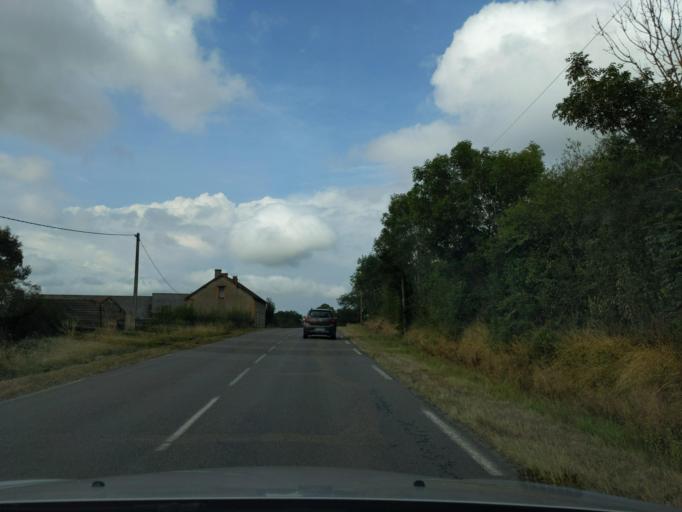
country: FR
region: Bourgogne
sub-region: Departement de Saone-et-Loire
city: Bourbon-Lancy
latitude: 46.6868
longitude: 3.8370
